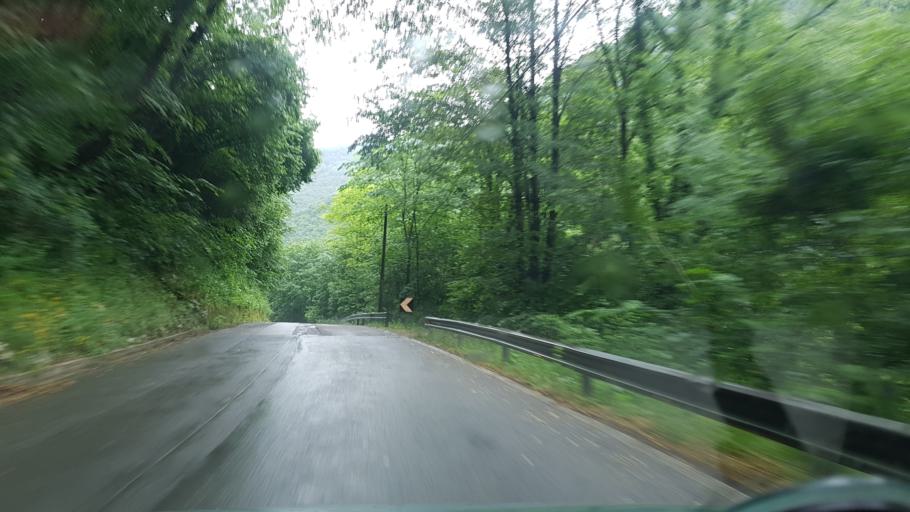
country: IT
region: Friuli Venezia Giulia
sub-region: Provincia di Udine
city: Nimis
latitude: 46.2376
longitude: 13.2894
